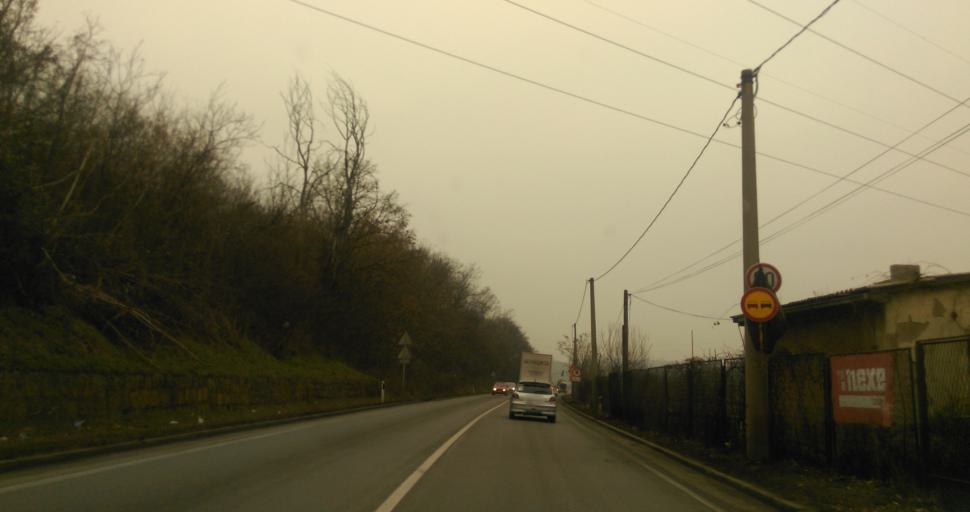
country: RS
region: Central Serbia
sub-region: Belgrade
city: Rakovica
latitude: 44.7177
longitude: 20.4646
